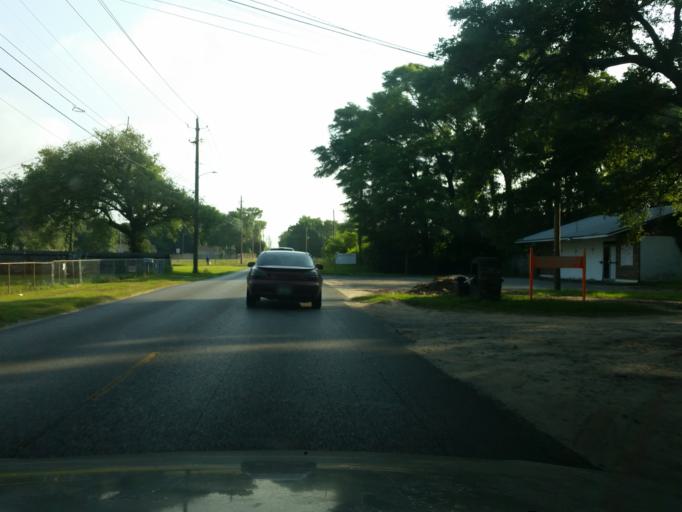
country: US
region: Florida
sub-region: Escambia County
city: West Pensacola
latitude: 30.4340
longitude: -87.2630
